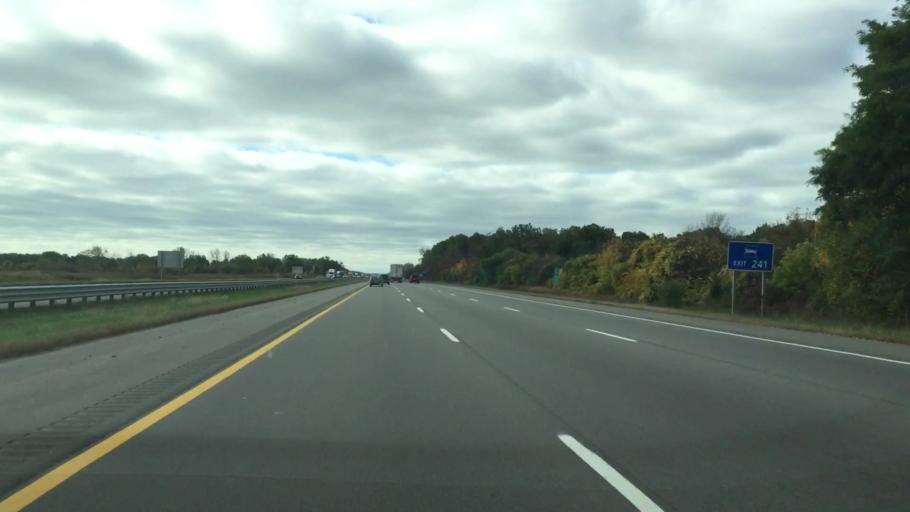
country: US
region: Michigan
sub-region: Macomb County
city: New Haven
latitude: 42.6592
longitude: -82.8318
